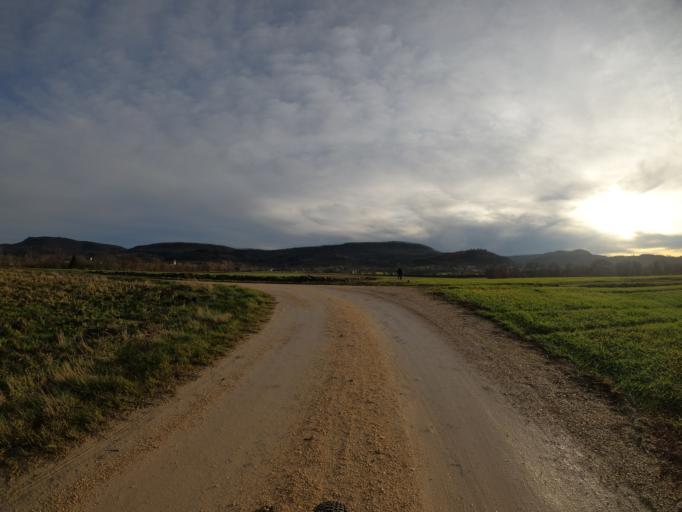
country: DE
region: Baden-Wuerttemberg
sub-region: Regierungsbezirk Stuttgart
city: Durnau
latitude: 48.6481
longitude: 9.6254
